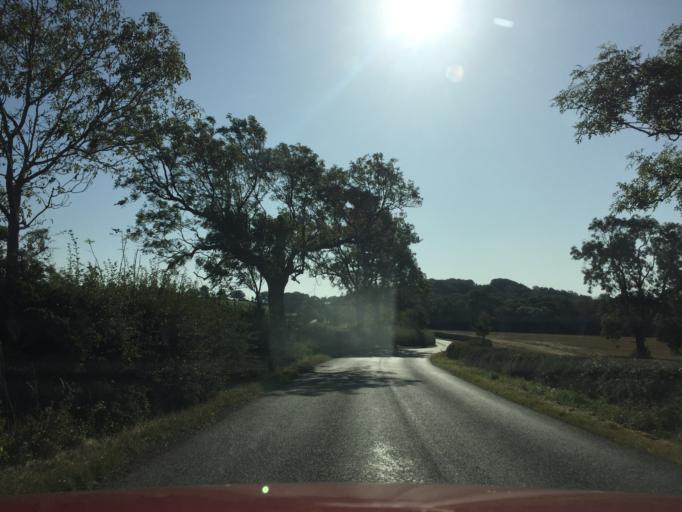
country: GB
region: England
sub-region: Leicestershire
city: Houghton on the Hill
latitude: 52.6391
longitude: -0.9611
